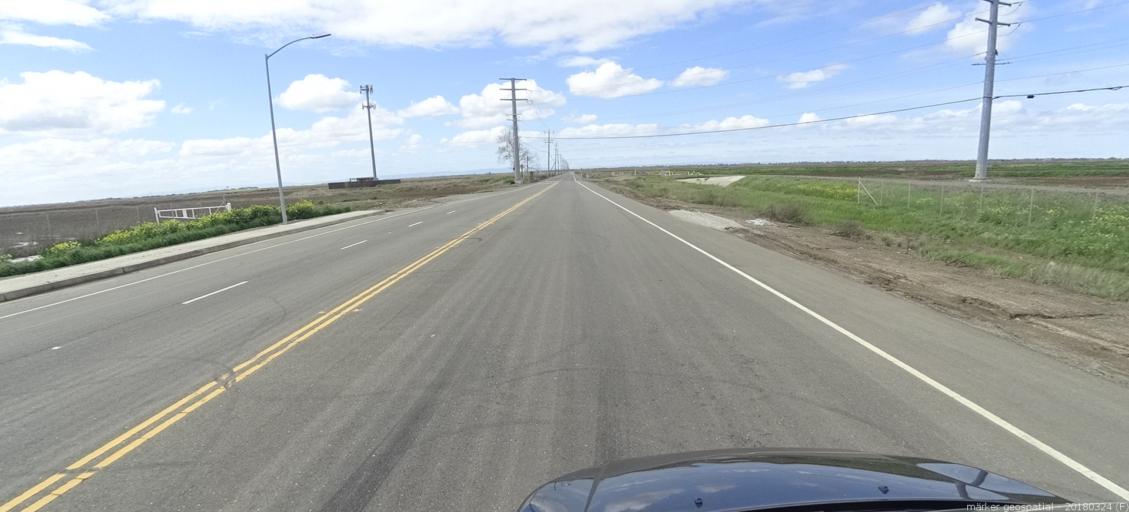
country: US
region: California
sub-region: Sacramento County
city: Elverta
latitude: 38.7144
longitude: -121.5449
